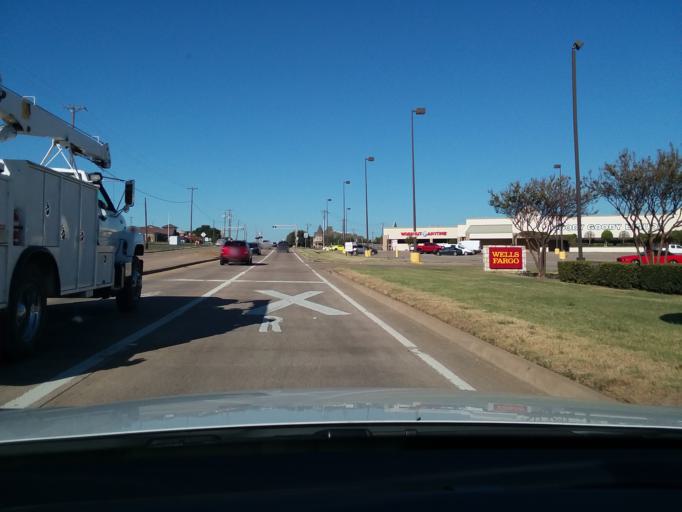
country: US
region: Texas
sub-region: Denton County
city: Highland Village
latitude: 33.0717
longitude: -97.0466
